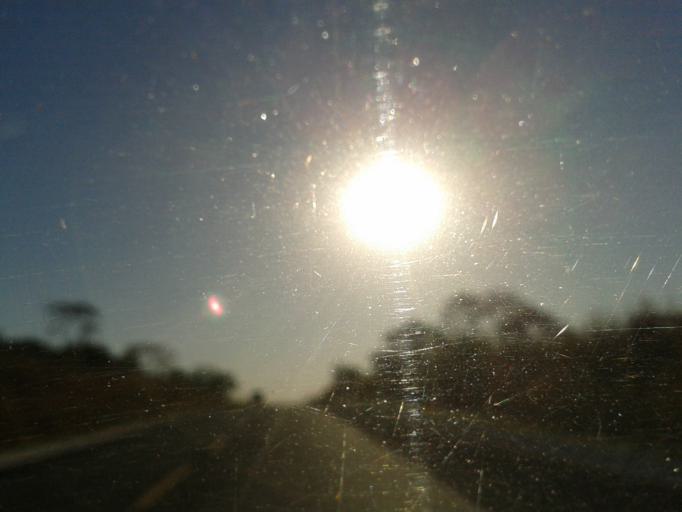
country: BR
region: Minas Gerais
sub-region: Santa Vitoria
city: Santa Vitoria
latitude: -19.1242
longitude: -50.2807
